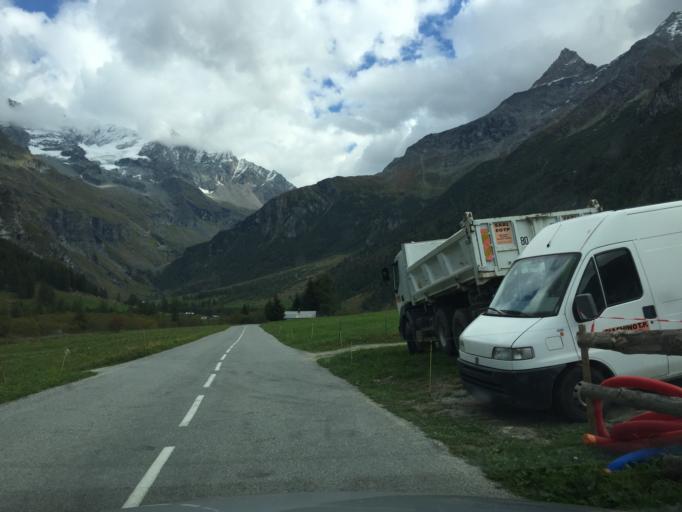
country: FR
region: Rhone-Alpes
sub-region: Departement de la Savoie
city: Belle-Plagne
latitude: 45.5235
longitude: 6.7936
